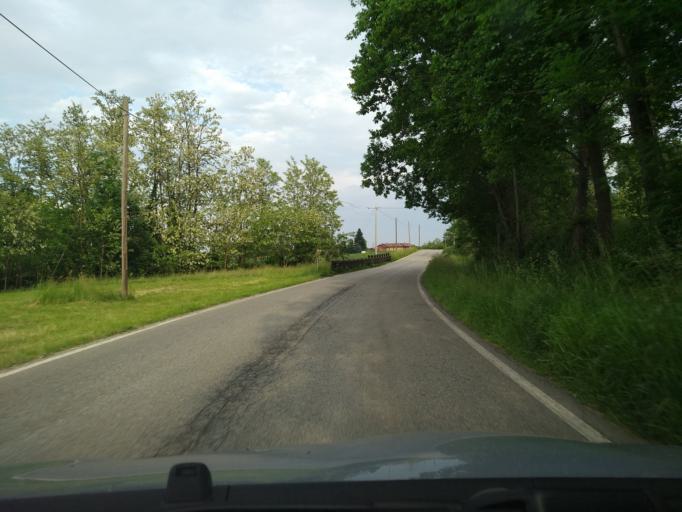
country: IT
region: Piedmont
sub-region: Provincia di Torino
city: Roletto
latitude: 44.9103
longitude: 7.3431
